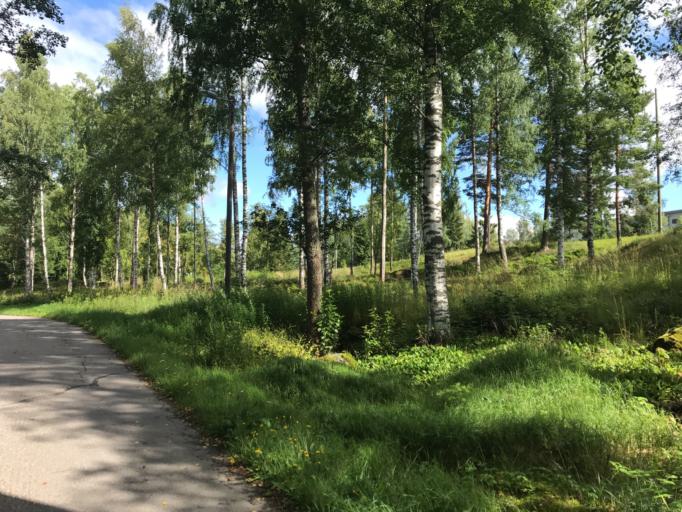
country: FI
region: Pirkanmaa
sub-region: Etelae-Pirkanmaa
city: Valkeakoski
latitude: 61.2669
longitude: 24.0485
